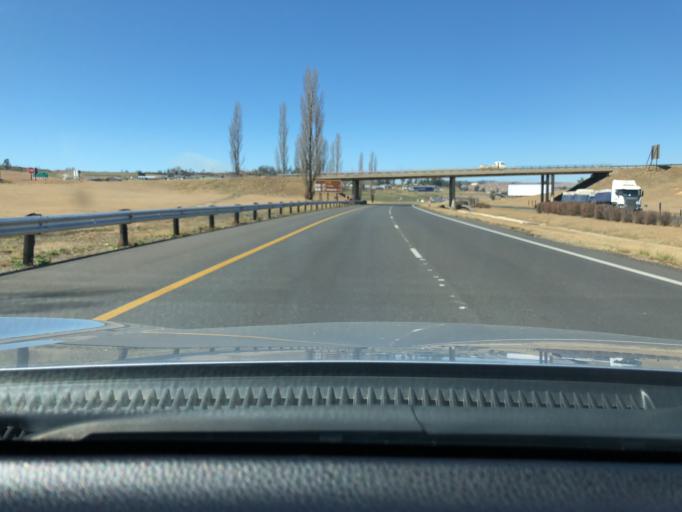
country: ZA
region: KwaZulu-Natal
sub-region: uMgungundlovu District Municipality
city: Mooirivier
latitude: -29.1925
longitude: 29.9931
